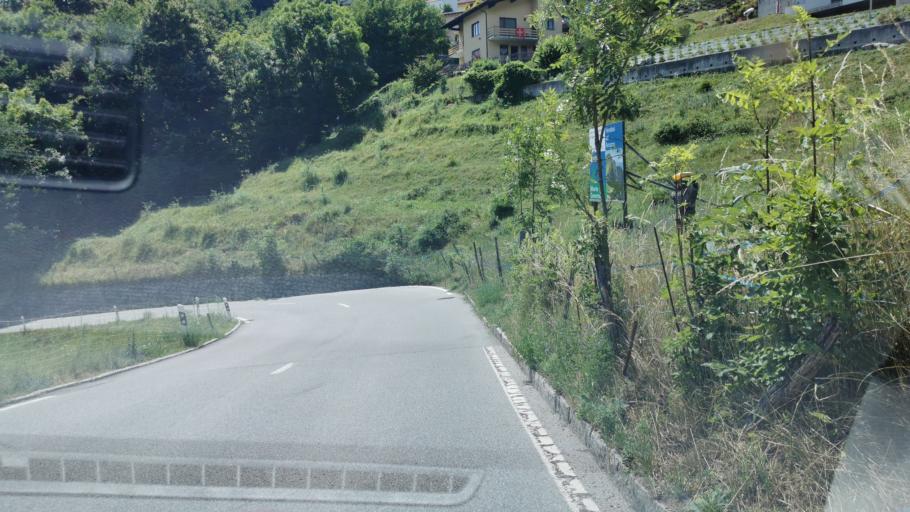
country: IT
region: Lombardy
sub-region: Provincia di Como
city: Campione
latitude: 45.9557
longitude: 8.9840
